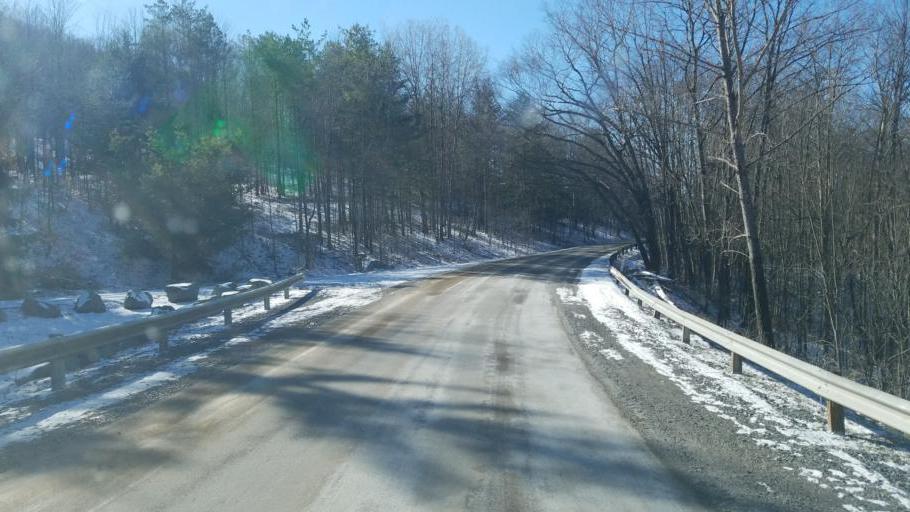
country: US
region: New York
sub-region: Allegany County
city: Wellsville
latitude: 42.1429
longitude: -77.9462
